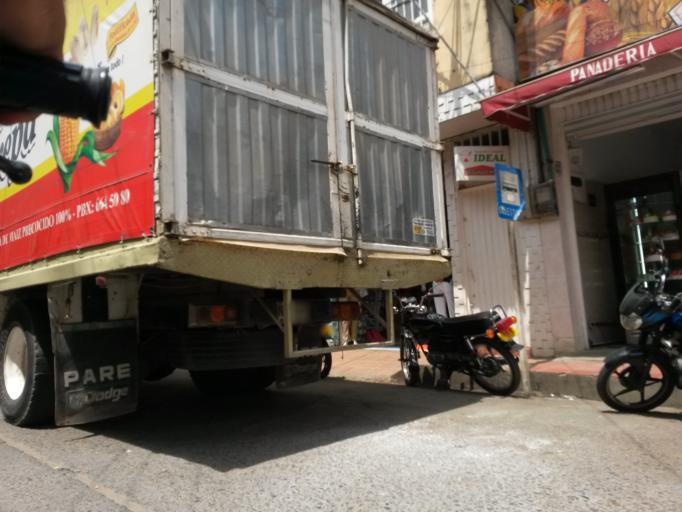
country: CO
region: Cauca
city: Santander de Quilichao
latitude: 3.0078
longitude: -76.4851
